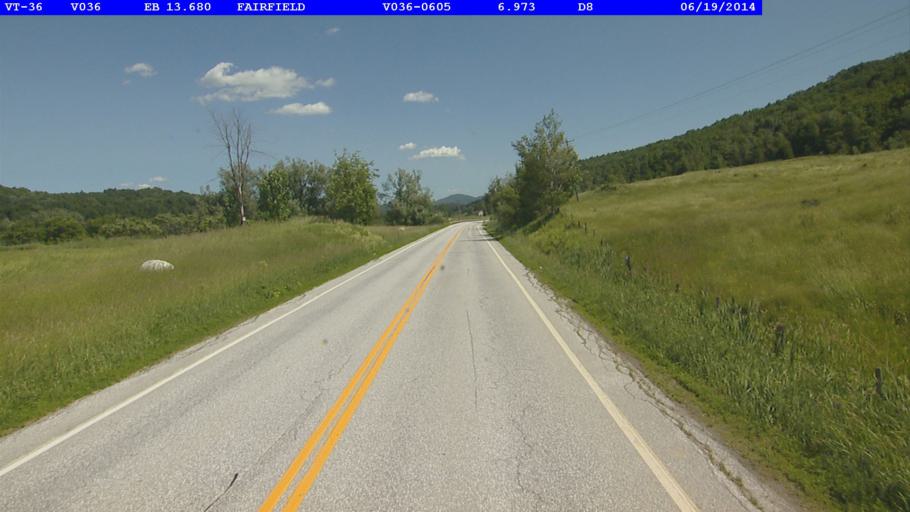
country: US
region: Vermont
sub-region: Franklin County
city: Enosburg Falls
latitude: 44.8048
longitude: -72.8977
